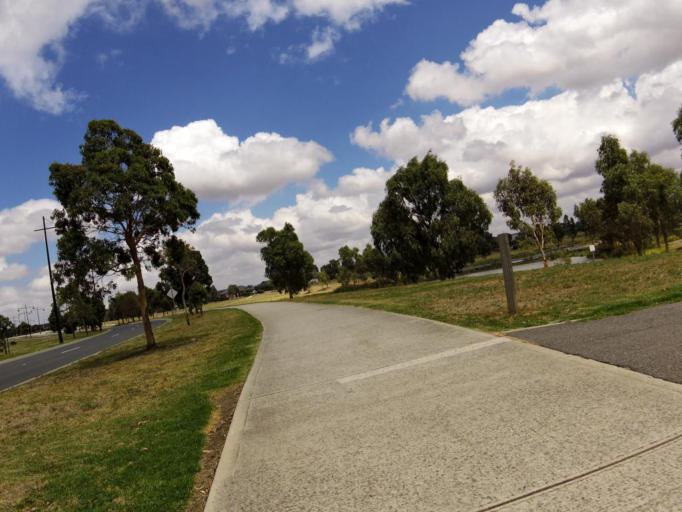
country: AU
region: Victoria
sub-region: Hume
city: Craigieburn
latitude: -37.5838
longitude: 144.9194
